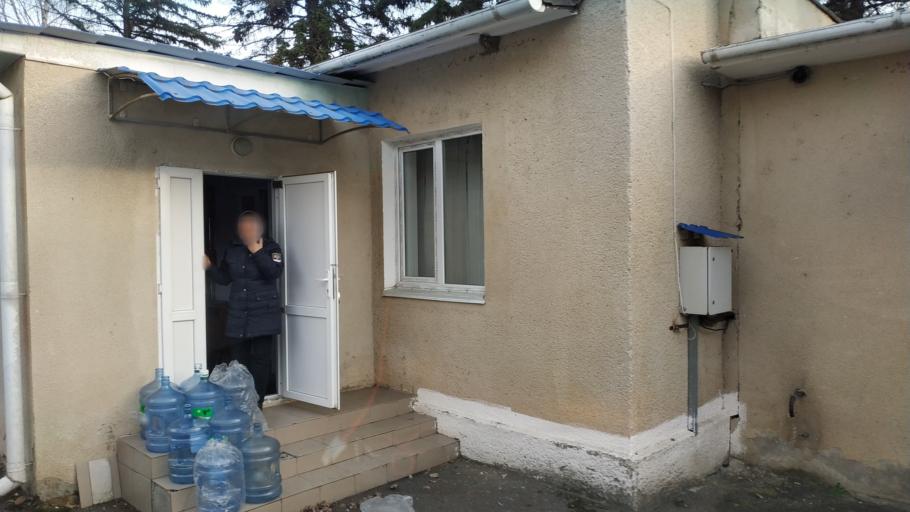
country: RO
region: Vaslui
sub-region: Comuna Dranceni
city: Rasesti
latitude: 46.7943
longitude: 28.1599
